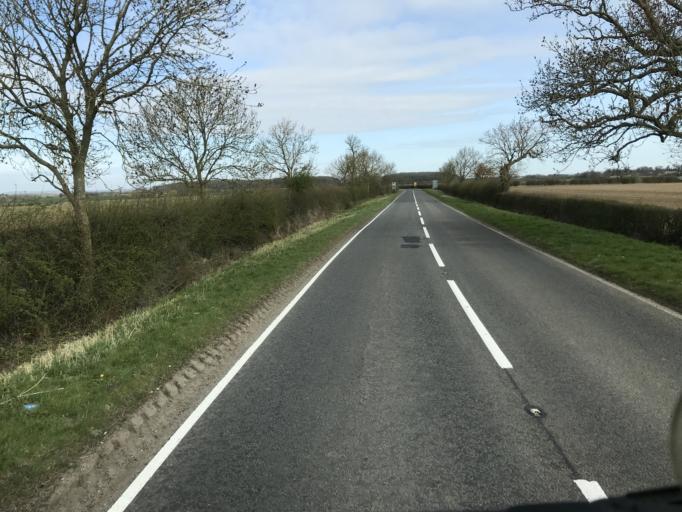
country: GB
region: England
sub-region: Lincolnshire
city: Market Rasen
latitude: 53.3954
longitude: -0.4182
